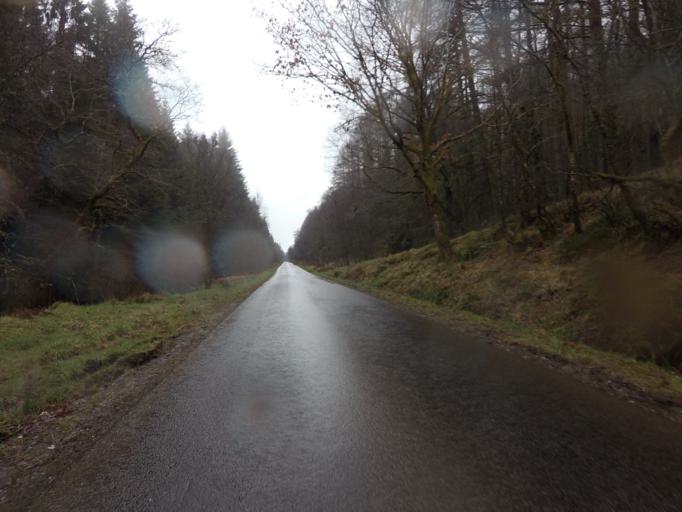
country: GB
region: Scotland
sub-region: West Dunbartonshire
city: Balloch
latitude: 56.2275
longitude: -4.5550
